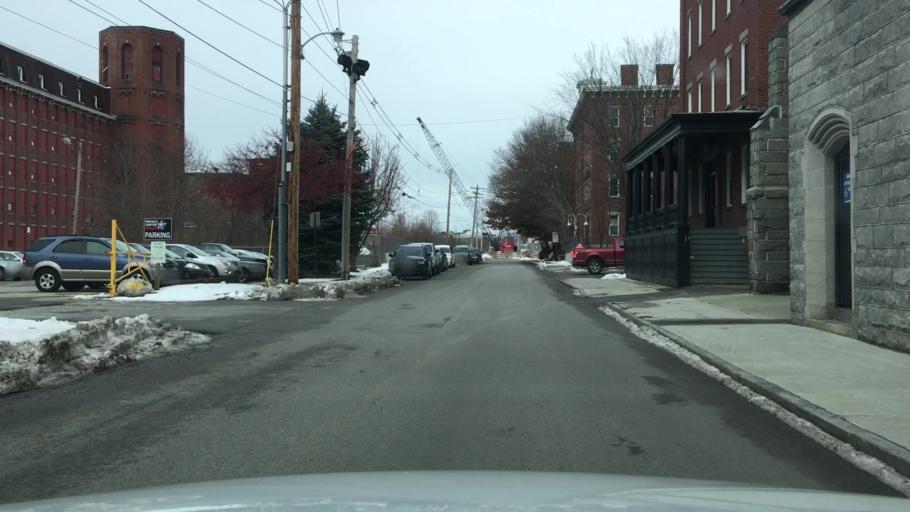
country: US
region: Maine
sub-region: Androscoggin County
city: Lewiston
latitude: 44.0915
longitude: -70.2194
